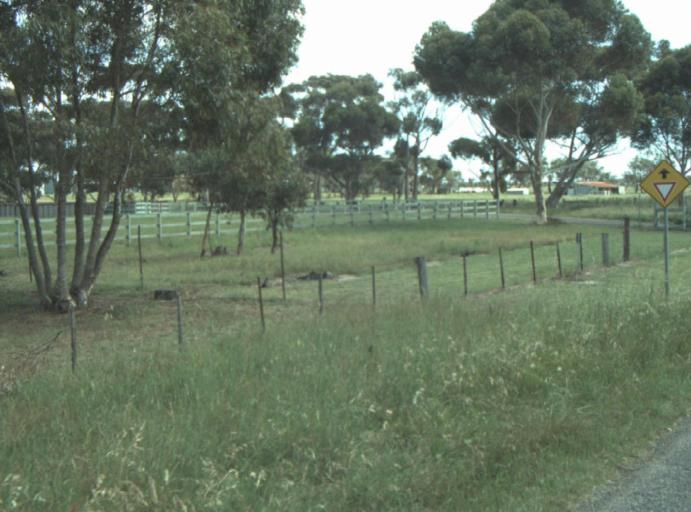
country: AU
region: Victoria
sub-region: Greater Geelong
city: Lara
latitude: -38.0569
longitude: 144.4274
